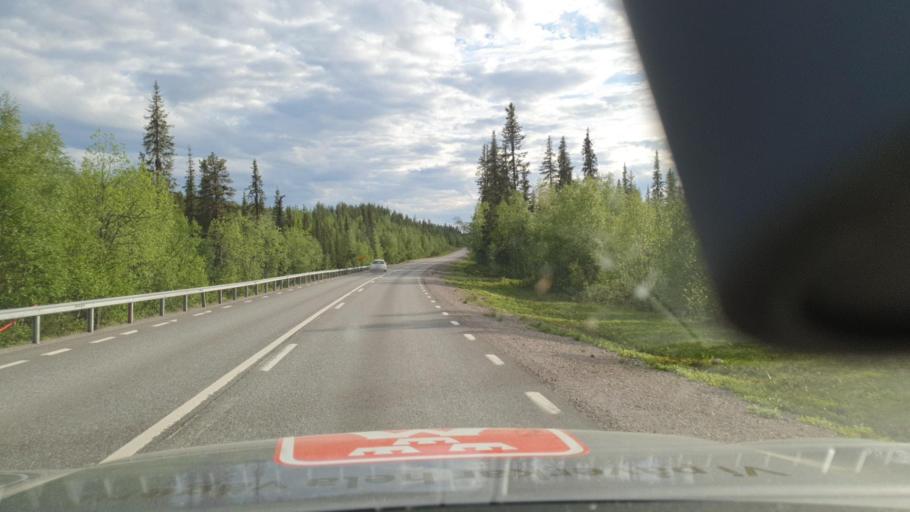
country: SE
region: Norrbotten
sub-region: Gallivare Kommun
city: Malmberget
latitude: 67.2093
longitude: 21.0131
